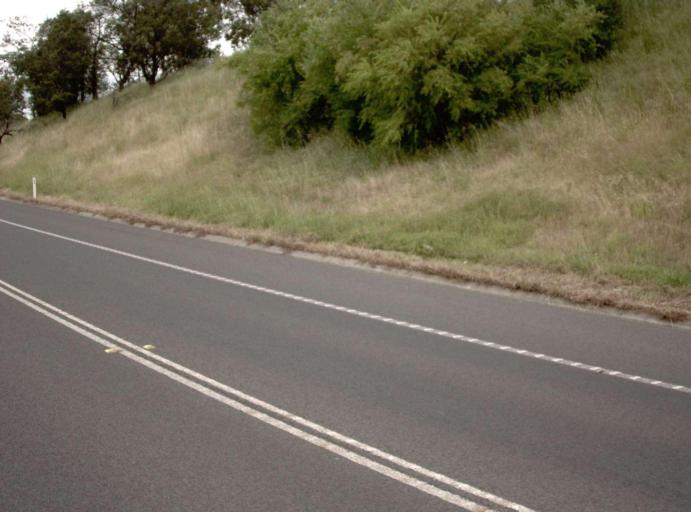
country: AU
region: Victoria
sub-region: Baw Baw
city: Warragul
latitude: -38.4470
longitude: 145.8937
